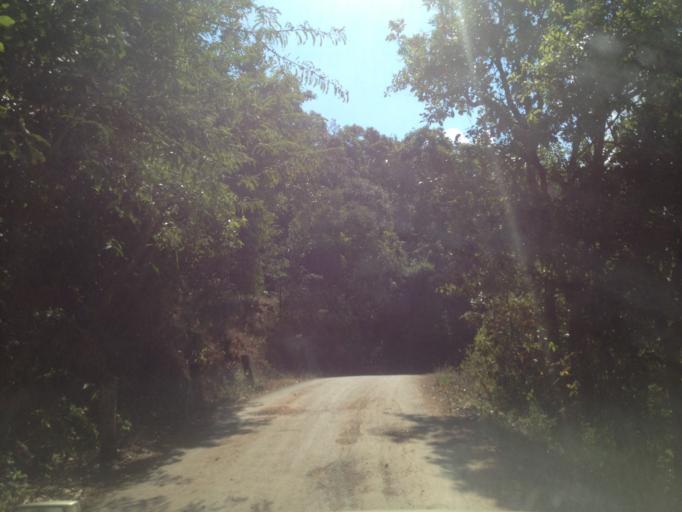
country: TH
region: Mae Hong Son
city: Ban Huai I Huak
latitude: 18.1116
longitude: 98.1635
